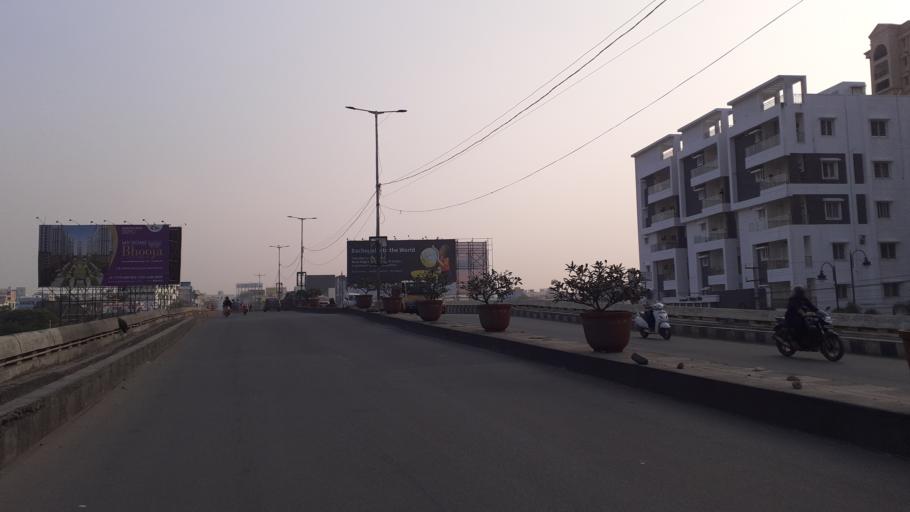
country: IN
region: Telangana
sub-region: Rangareddi
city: Kukatpalli
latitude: 17.4841
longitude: 78.3604
